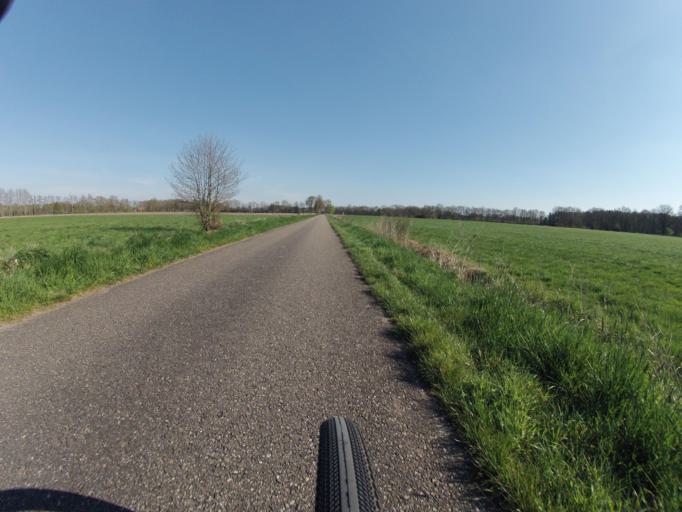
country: DE
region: Lower Saxony
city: Isterberg
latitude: 52.3527
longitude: 7.1617
